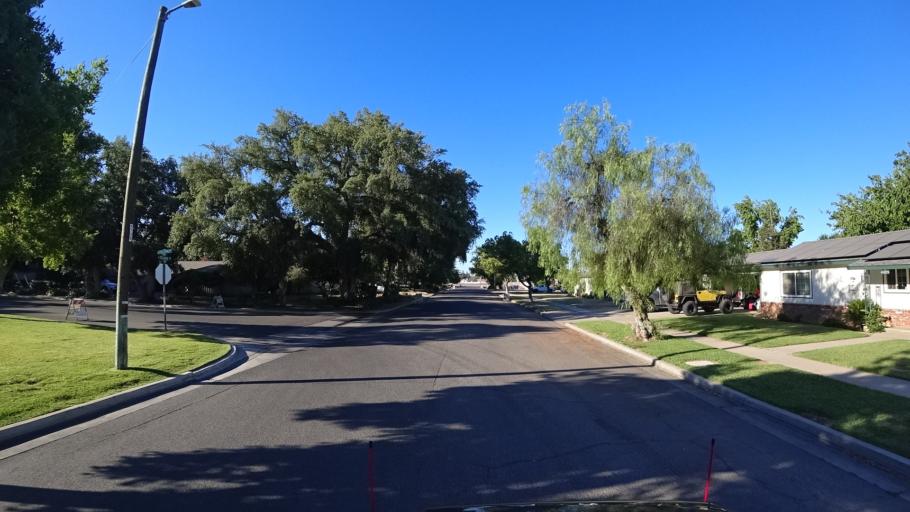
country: US
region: California
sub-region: Fresno County
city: Fresno
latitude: 36.7976
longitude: -119.8220
